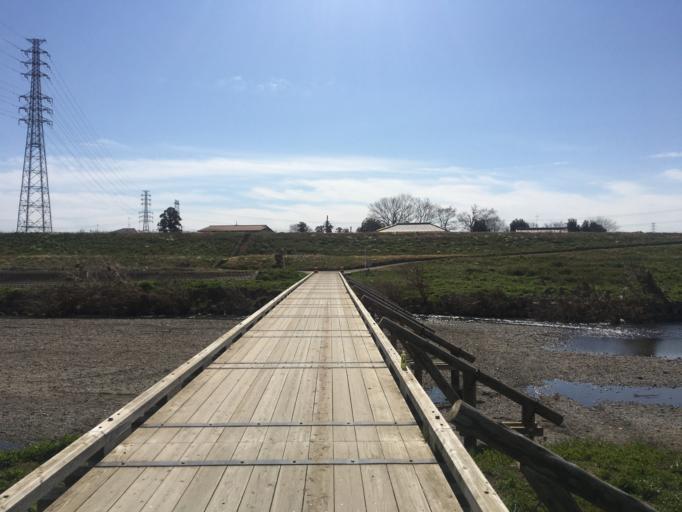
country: JP
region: Saitama
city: Sakado
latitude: 35.9891
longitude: 139.4086
